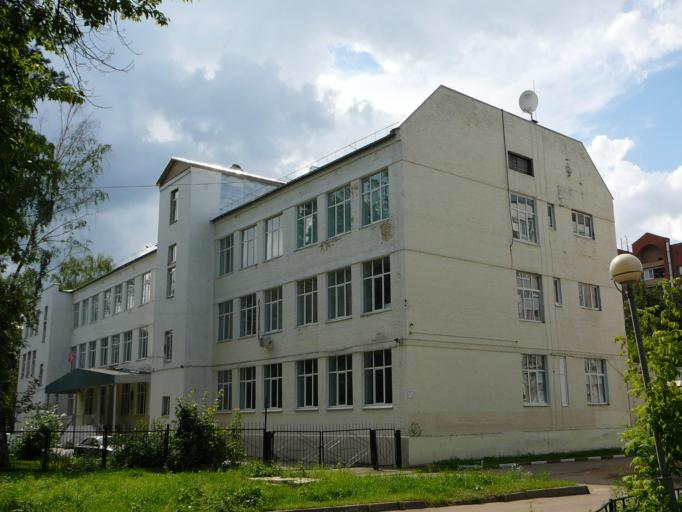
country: RU
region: Moskovskaya
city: Krasnogorsk
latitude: 55.8297
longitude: 37.3290
